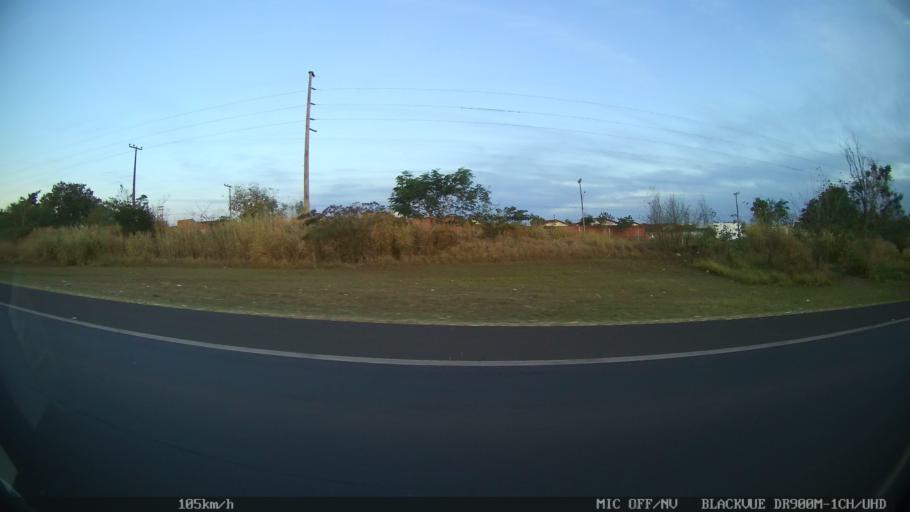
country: BR
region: Sao Paulo
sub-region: Catanduva
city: Catanduva
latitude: -21.1195
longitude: -48.9872
